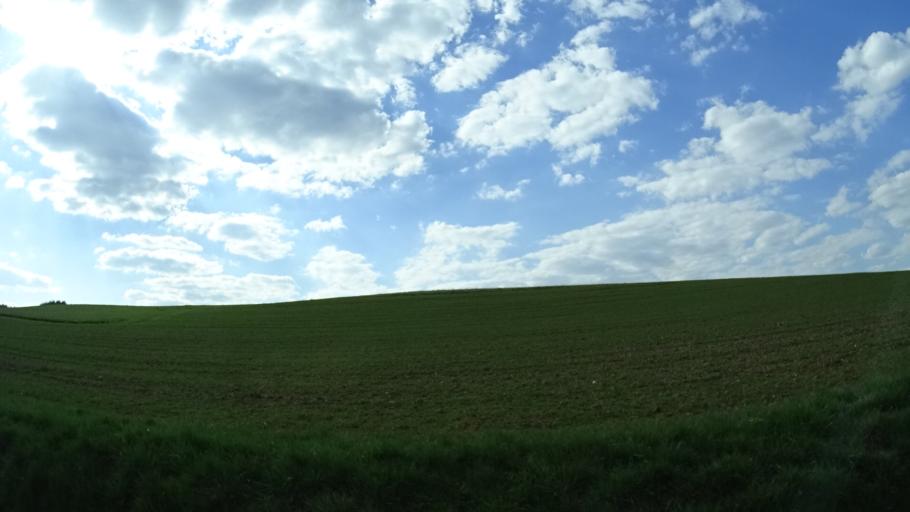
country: DE
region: Rheinland-Pfalz
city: Otzweiler
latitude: 49.7315
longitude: 7.5143
